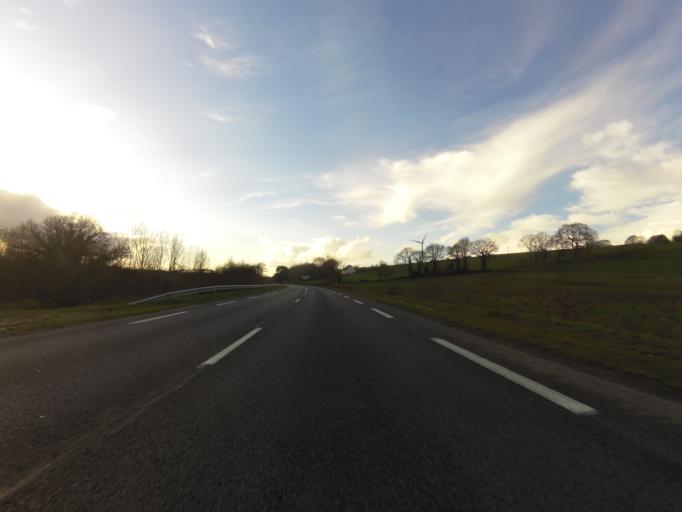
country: FR
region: Brittany
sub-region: Departement du Morbihan
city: Guegon
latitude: 47.9613
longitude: -2.5885
